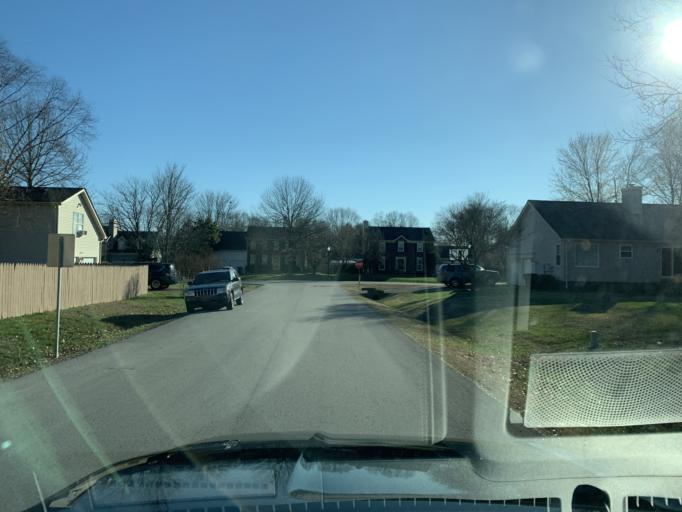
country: US
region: Tennessee
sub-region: Williamson County
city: Franklin
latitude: 35.8926
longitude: -86.8361
